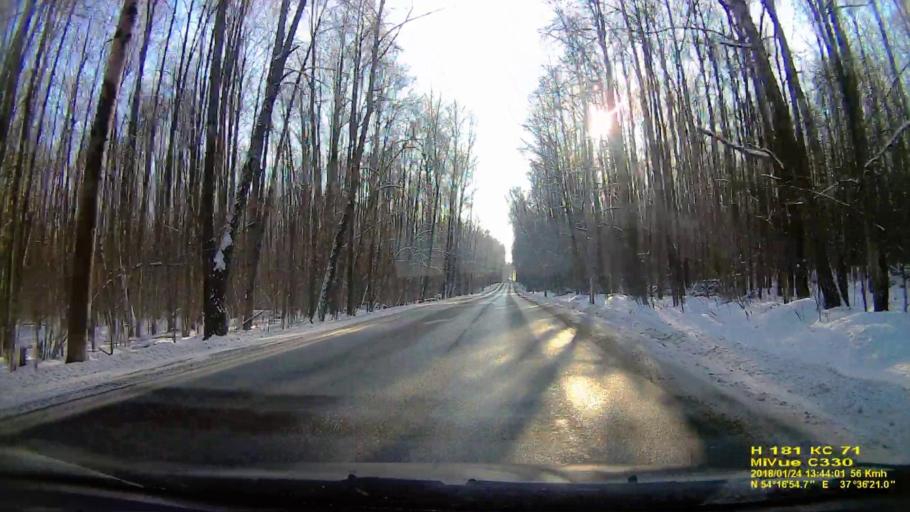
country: RU
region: Tula
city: Gorelki
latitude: 54.2817
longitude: 37.6058
